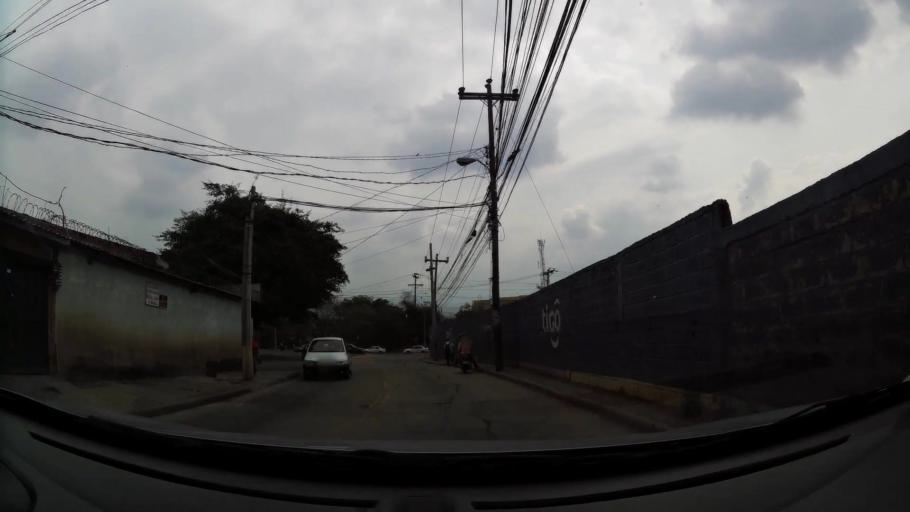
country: HN
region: Francisco Morazan
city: Tegucigalpa
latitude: 14.0920
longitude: -87.1656
